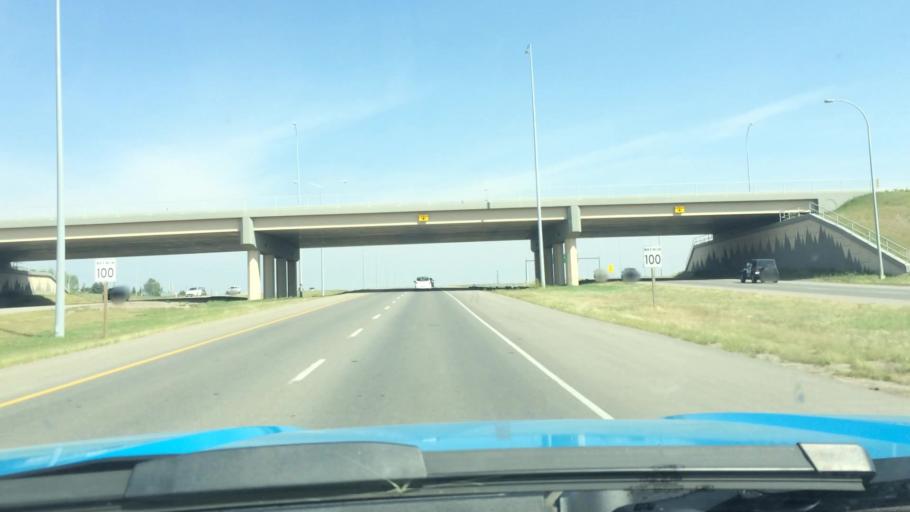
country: CA
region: Alberta
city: Okotoks
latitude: 50.8968
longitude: -113.9934
